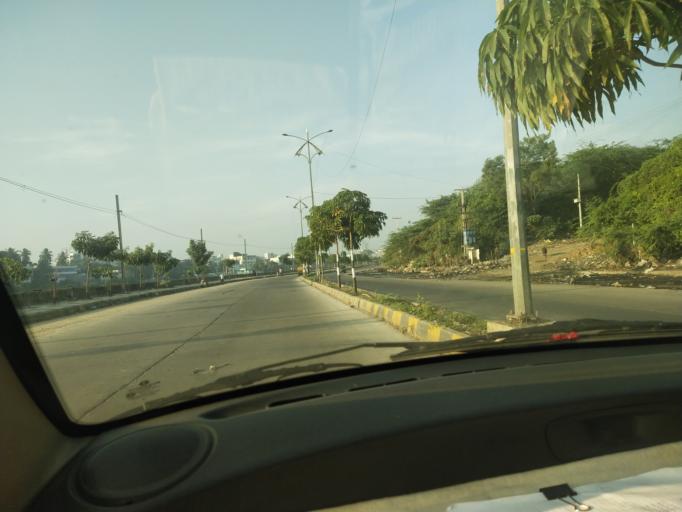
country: IN
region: Telangana
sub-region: Hyderabad
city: Hyderabad
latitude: 17.3629
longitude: 78.4546
